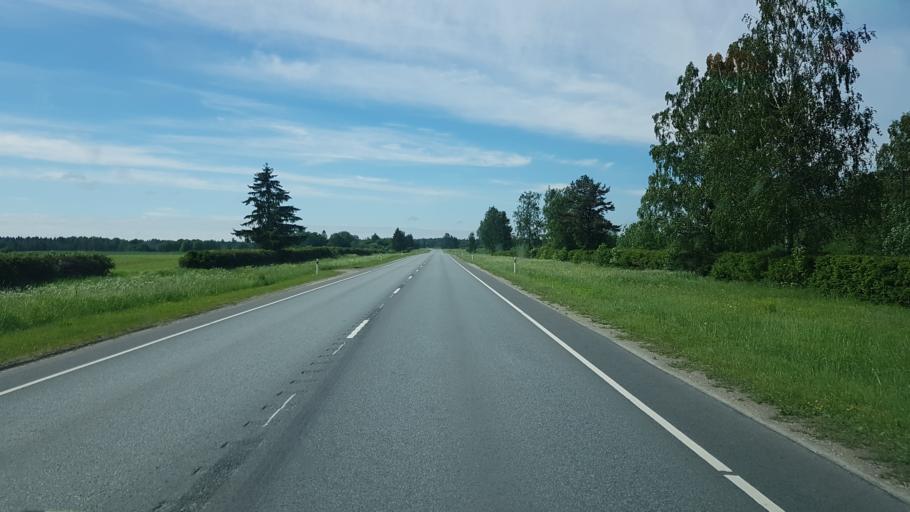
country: EE
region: Laeaene-Virumaa
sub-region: Kadrina vald
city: Kadrina
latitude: 59.3199
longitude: 26.0891
